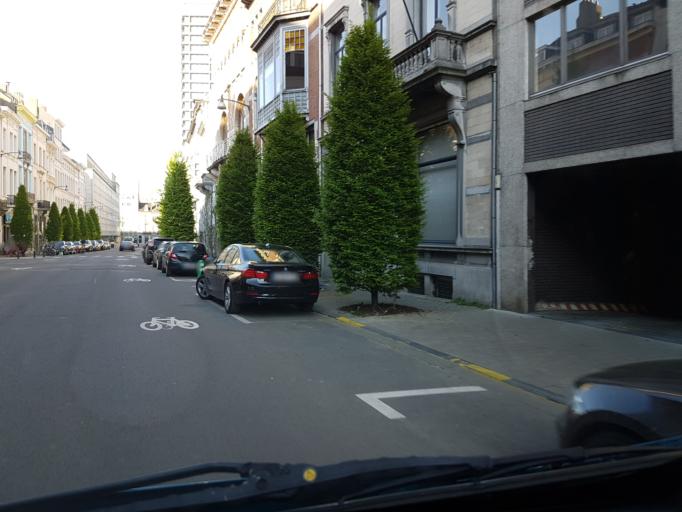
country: BE
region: Brussels Capital
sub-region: Bruxelles-Capitale
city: Brussels
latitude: 50.8277
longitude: 4.3592
